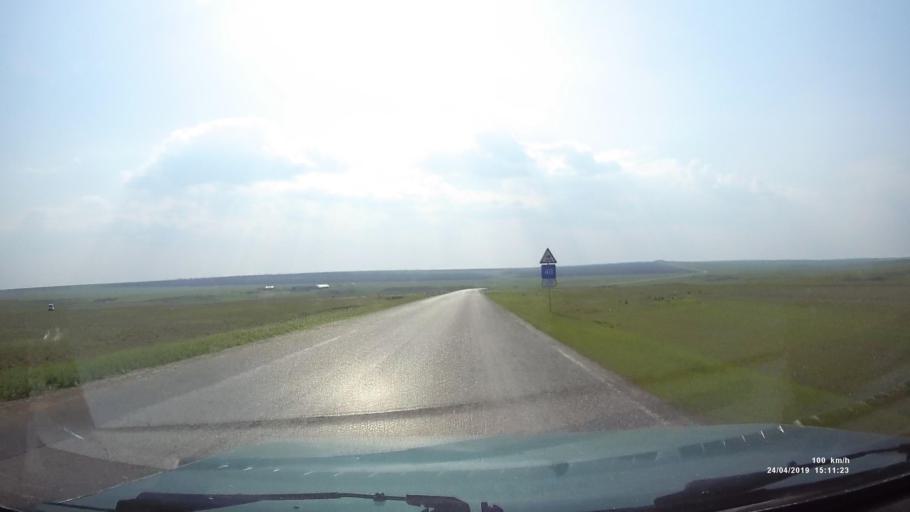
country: RU
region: Rostov
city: Remontnoye
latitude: 46.5446
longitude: 43.3220
